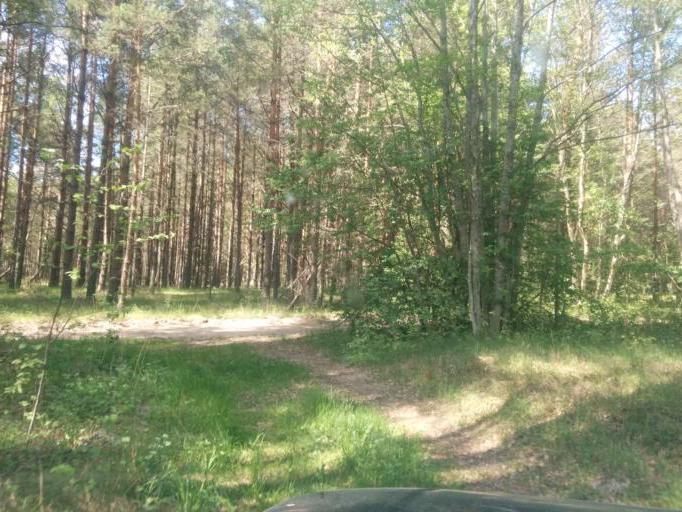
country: LV
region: Dundaga
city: Dundaga
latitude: 57.6242
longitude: 22.1055
